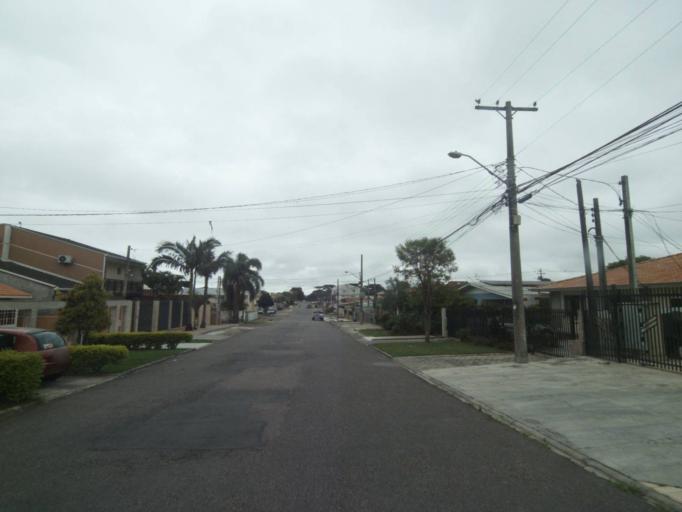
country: BR
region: Parana
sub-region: Sao Jose Dos Pinhais
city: Sao Jose dos Pinhais
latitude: -25.5434
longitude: -49.2822
